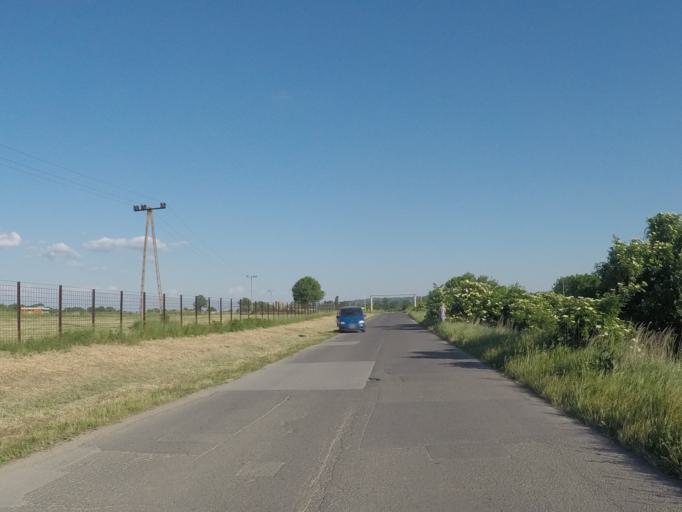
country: HU
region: Borsod-Abauj-Zemplen
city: Kazincbarcika
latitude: 48.2515
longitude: 20.6592
